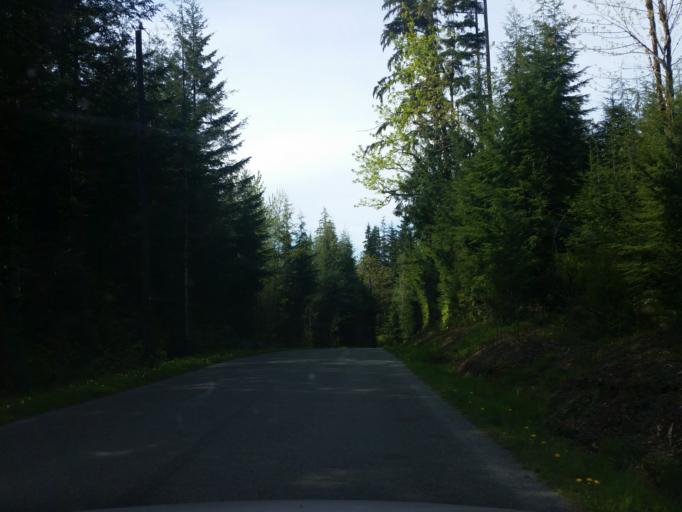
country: US
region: Washington
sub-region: Snohomish County
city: Woods Creek
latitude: 47.9877
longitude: -121.9024
